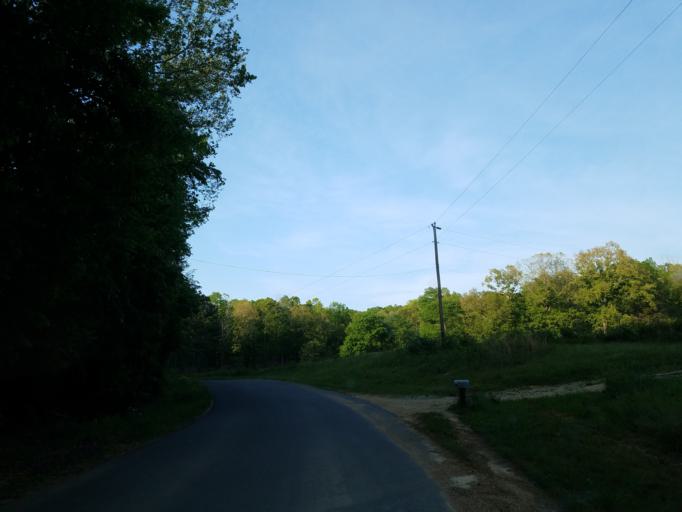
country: US
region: Georgia
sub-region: Whitfield County
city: Dalton
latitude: 34.6500
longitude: -85.0842
